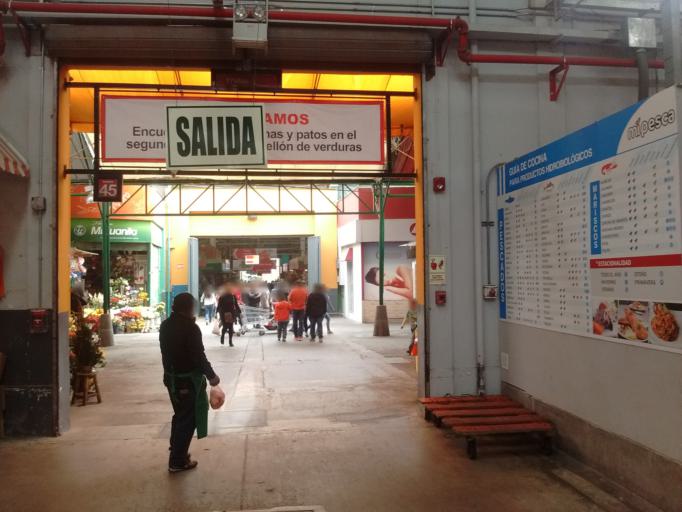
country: PE
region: Callao
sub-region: Callao
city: Callao
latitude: -12.0475
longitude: -77.1110
